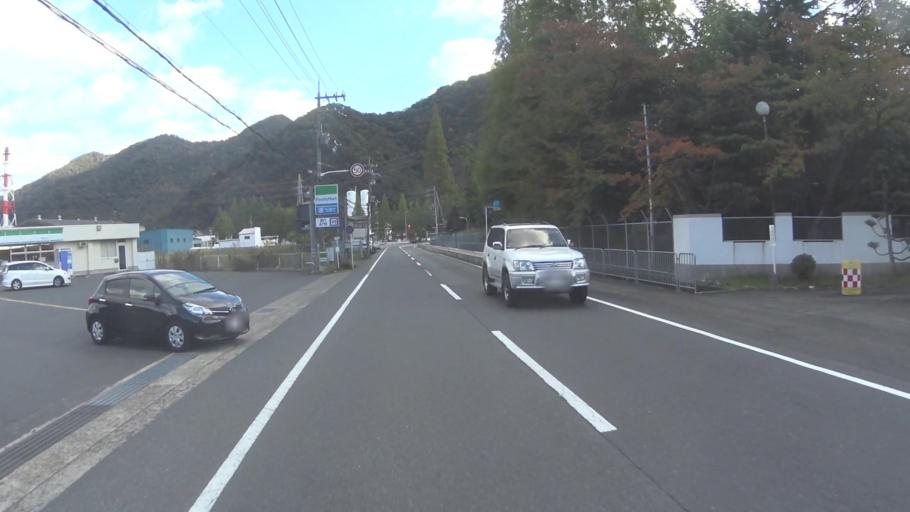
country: JP
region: Kyoto
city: Maizuru
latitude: 35.4997
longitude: 135.4044
